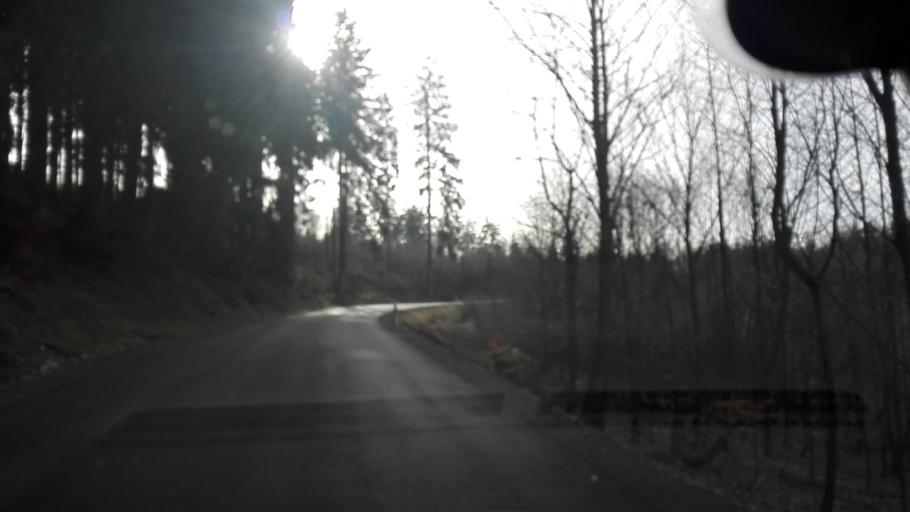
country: DE
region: North Rhine-Westphalia
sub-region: Regierungsbezirk Arnsberg
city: Schmallenberg
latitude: 51.1364
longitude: 8.3334
